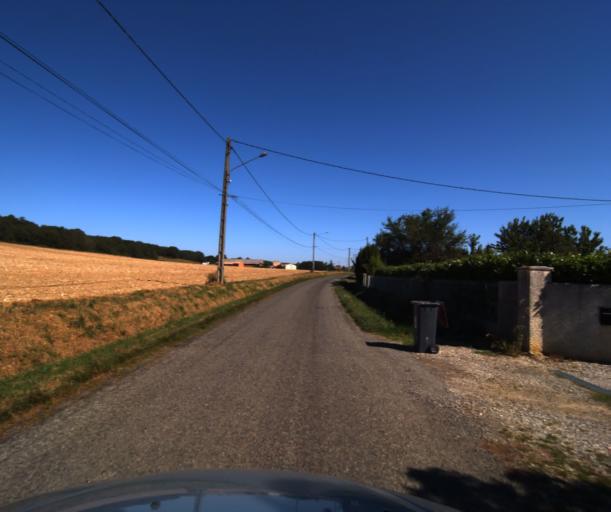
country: FR
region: Midi-Pyrenees
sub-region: Departement de la Haute-Garonne
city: Eaunes
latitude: 43.4143
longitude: 1.3539
